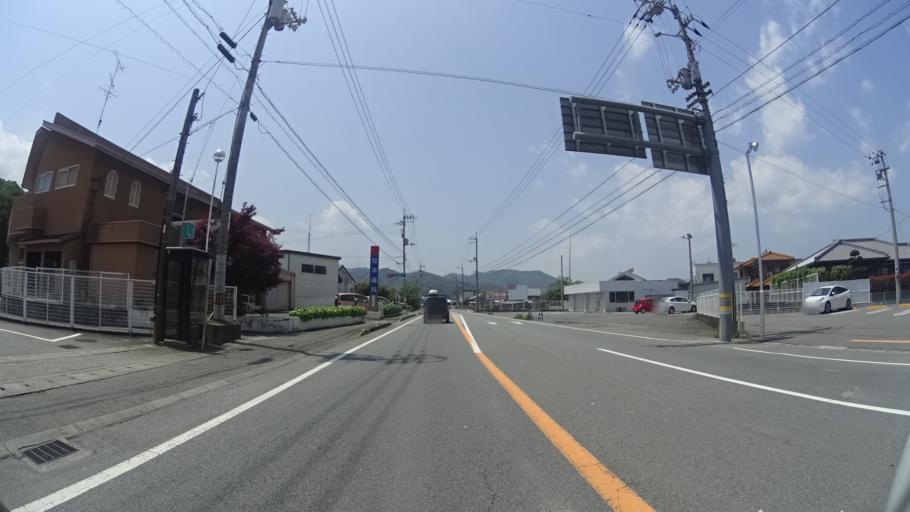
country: JP
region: Tokushima
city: Wakimachi
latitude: 34.0570
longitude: 134.2382
